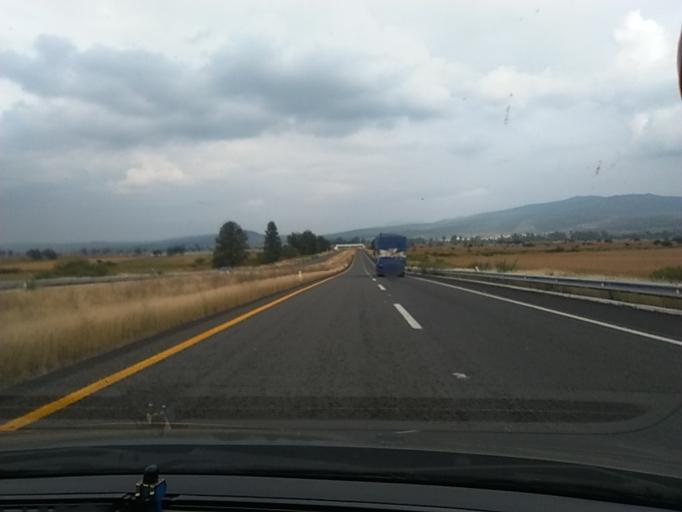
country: MX
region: Michoacan
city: Ecuandureo
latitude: 20.1760
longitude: -102.2412
